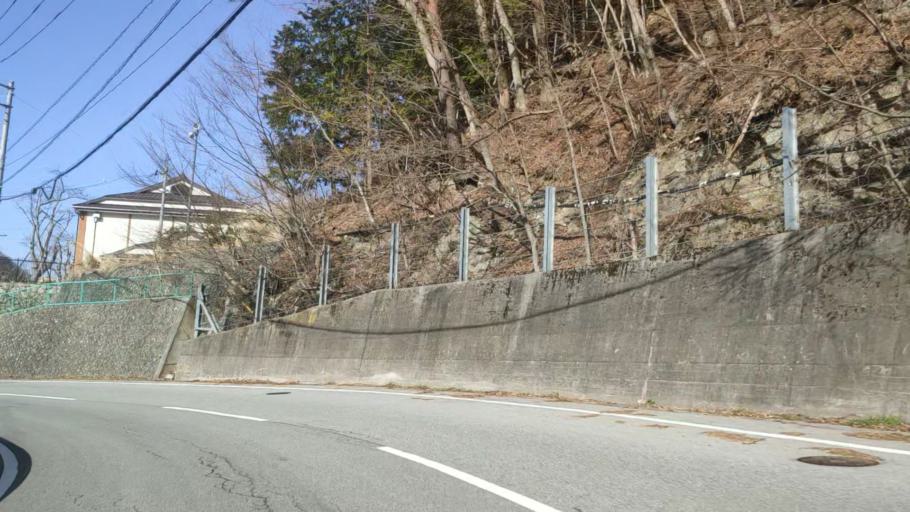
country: JP
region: Yamanashi
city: Fujikawaguchiko
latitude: 35.5554
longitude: 138.6719
